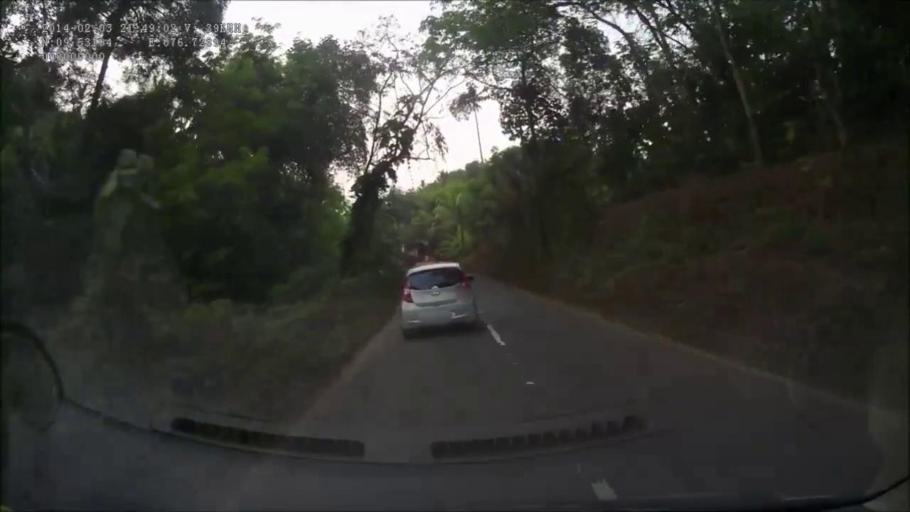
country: IN
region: Kerala
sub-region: Kottayam
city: Erattupetta
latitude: 9.5308
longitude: 76.7290
